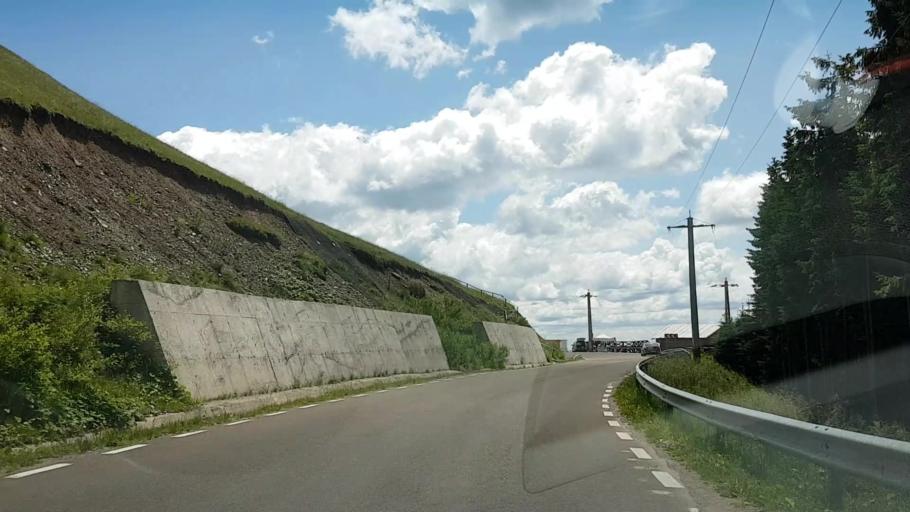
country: RO
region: Suceava
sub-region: Municipiul Campulung Moldovenesc
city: Campulung Moldovenesc
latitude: 47.4543
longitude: 25.5420
